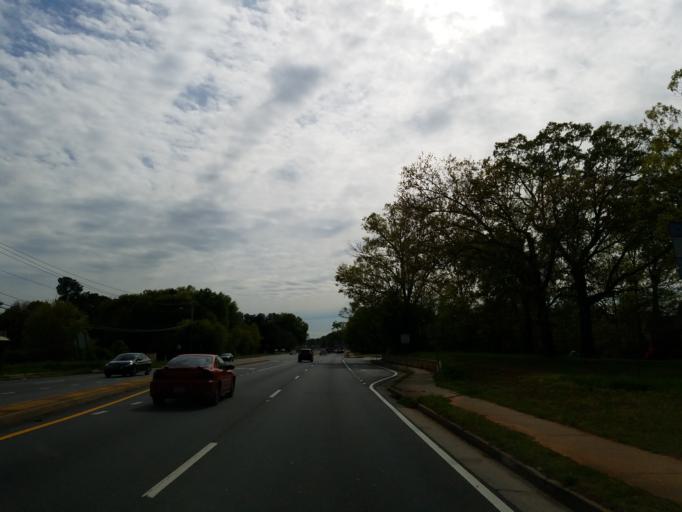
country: US
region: Georgia
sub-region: Cobb County
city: Fair Oaks
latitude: 33.9056
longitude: -84.5637
